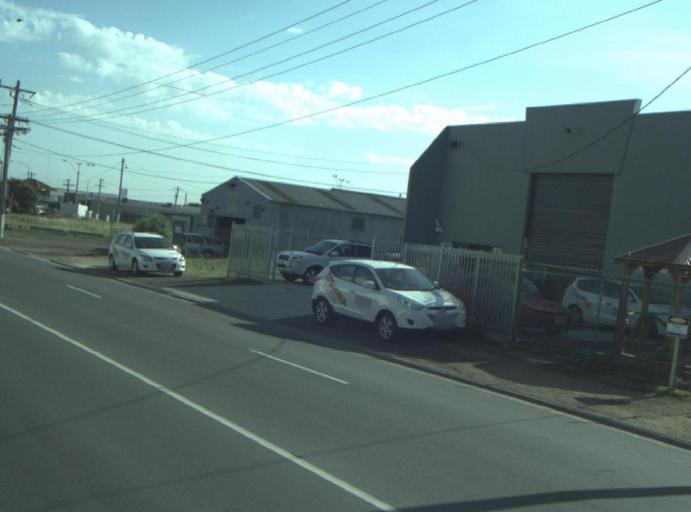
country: AU
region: Victoria
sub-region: Greater Geelong
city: Bell Park
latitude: -38.1134
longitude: 144.3494
